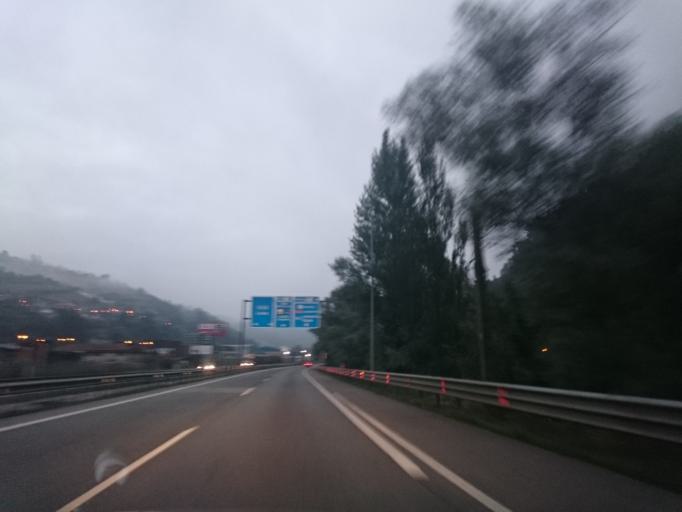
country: ES
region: Asturias
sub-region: Province of Asturias
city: Mieres
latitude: 43.2689
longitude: -5.8018
